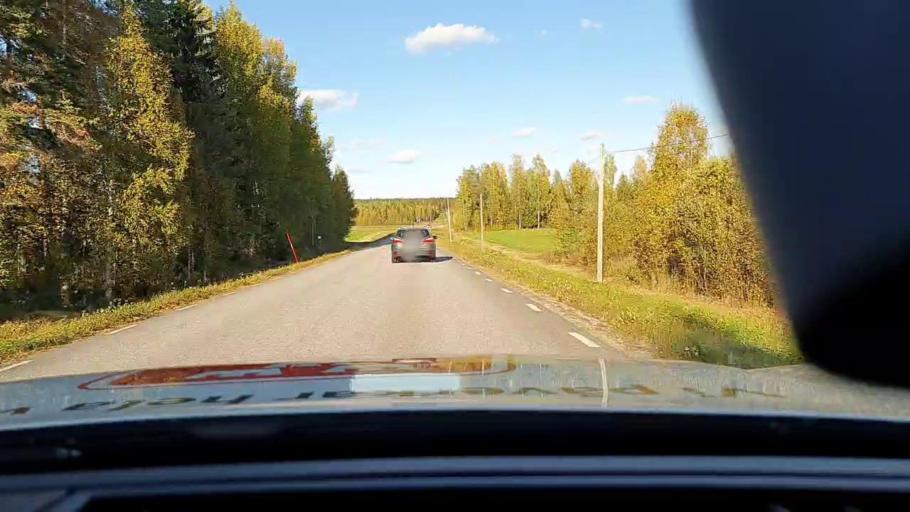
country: SE
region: Norrbotten
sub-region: Pitea Kommun
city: Norrfjarden
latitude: 65.5101
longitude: 21.4886
